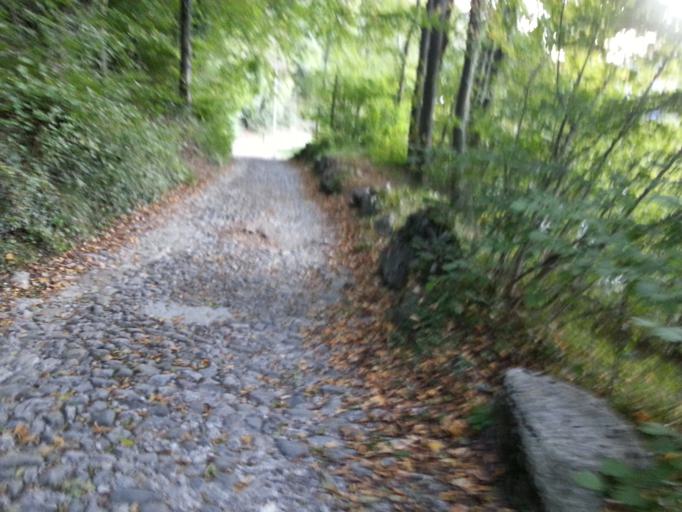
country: IT
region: Lombardy
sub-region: Provincia di Lecco
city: Barzio
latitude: 45.9550
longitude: 9.4660
